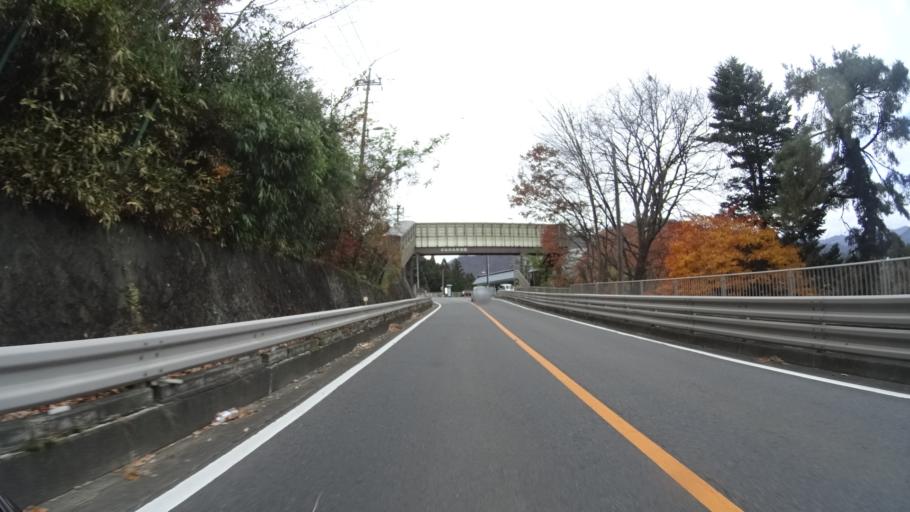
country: JP
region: Gunma
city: Nakanojomachi
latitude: 36.7278
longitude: 138.8941
